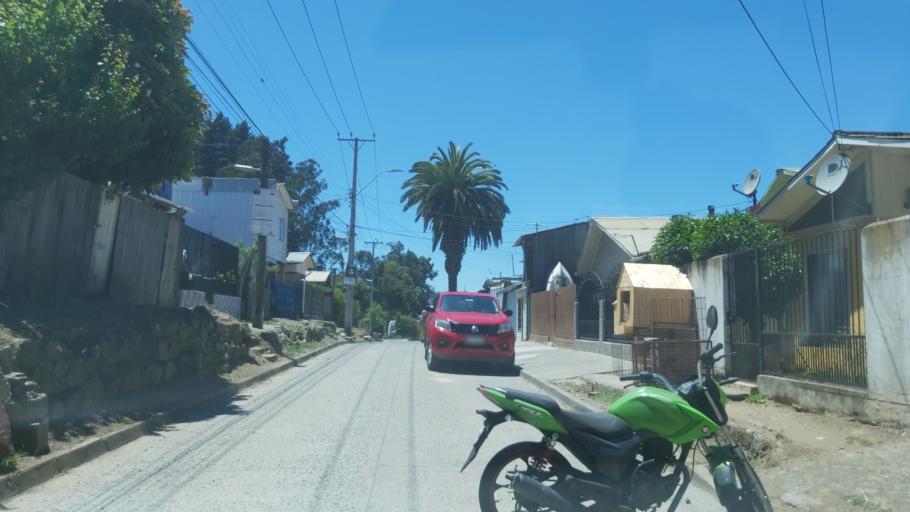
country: CL
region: Maule
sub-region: Provincia de Talca
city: Constitucion
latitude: -35.3254
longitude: -72.4133
